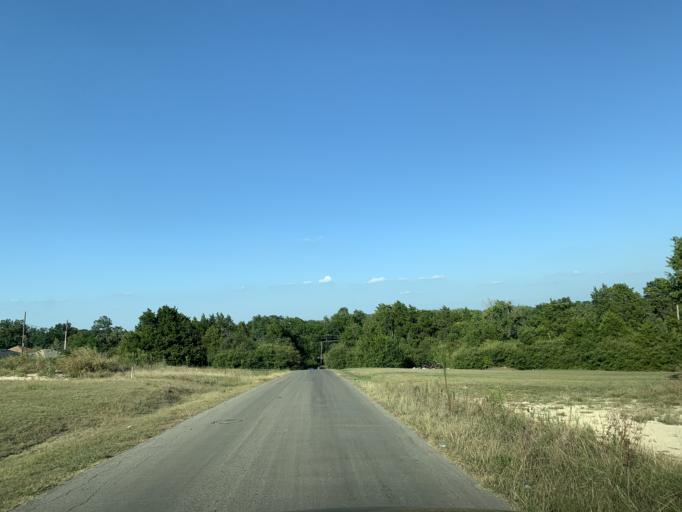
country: US
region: Texas
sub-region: Dallas County
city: Hutchins
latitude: 32.6723
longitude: -96.7775
